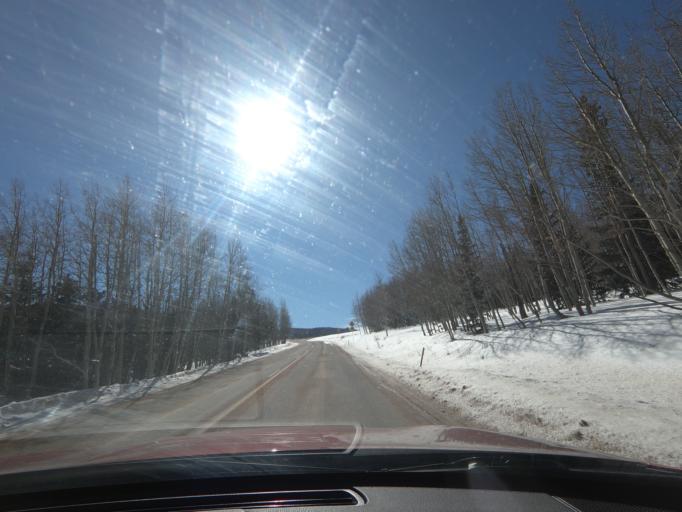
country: US
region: Colorado
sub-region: Teller County
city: Cripple Creek
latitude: 38.7338
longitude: -105.1190
